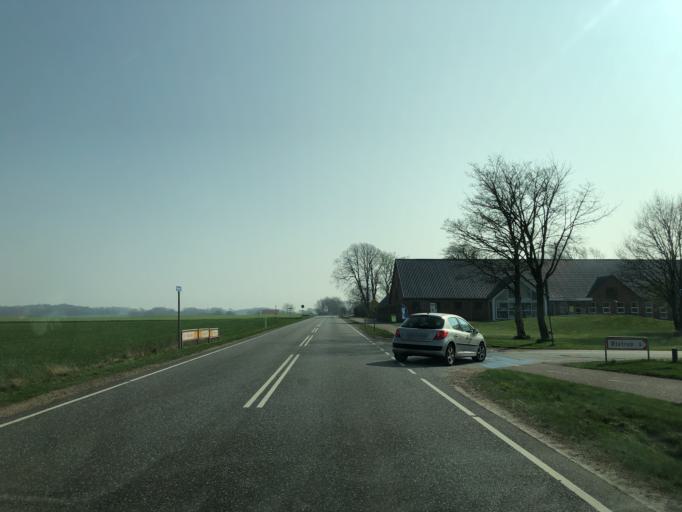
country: DK
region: Central Jutland
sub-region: Ringkobing-Skjern Kommune
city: Videbaek
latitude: 56.1195
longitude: 8.5029
